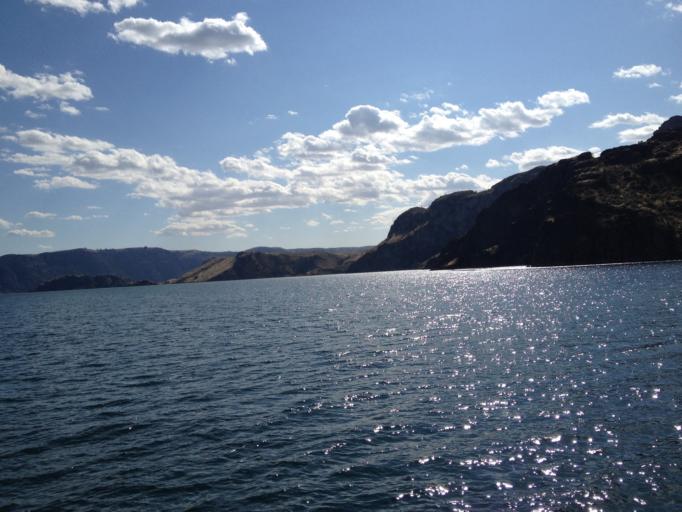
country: US
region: Washington
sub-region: Okanogan County
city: Coulee Dam
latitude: 47.9451
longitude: -118.6906
